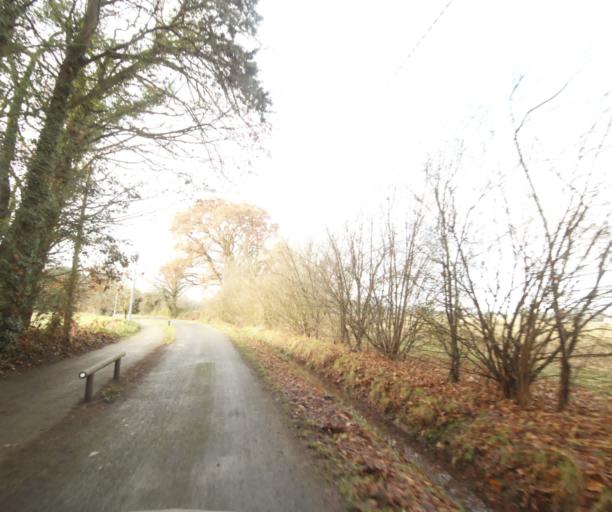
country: FR
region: Midi-Pyrenees
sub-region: Departement de la Haute-Garonne
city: Villemur-sur-Tarn
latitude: 43.8550
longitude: 1.4941
